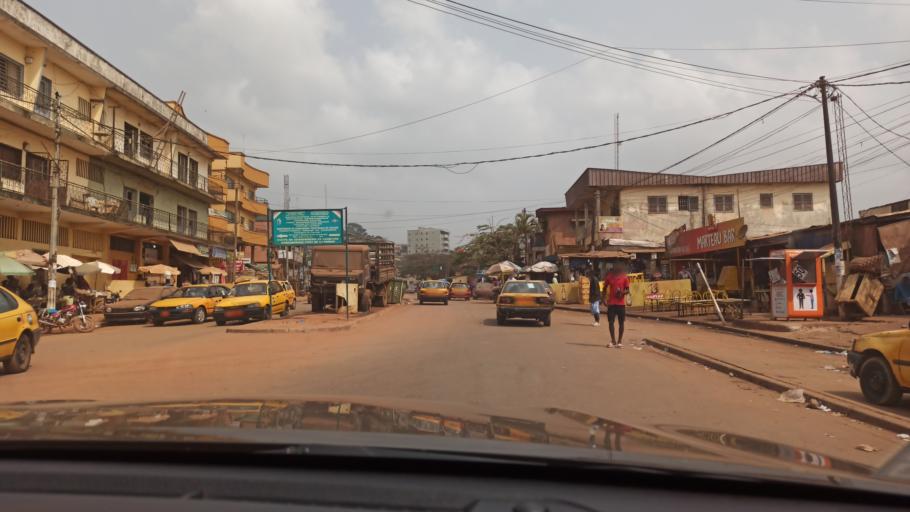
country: CM
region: Centre
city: Yaounde
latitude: 3.8849
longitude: 11.4921
